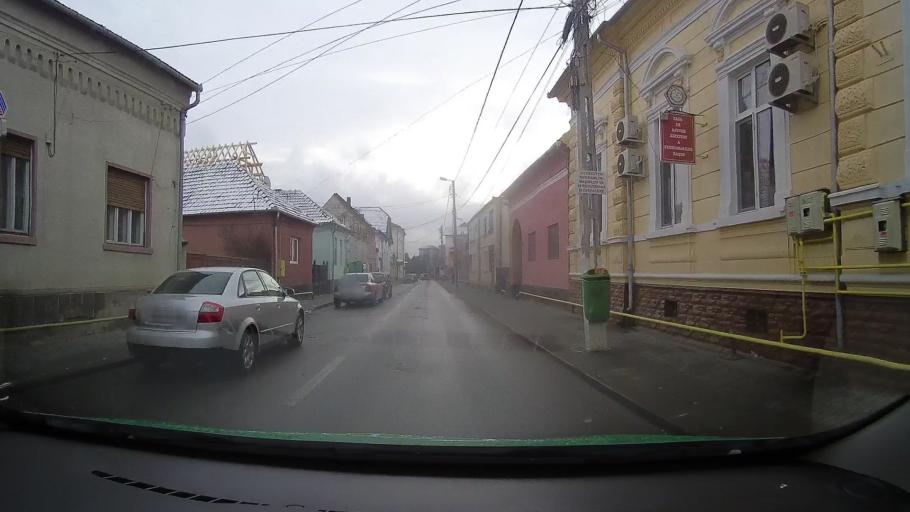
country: RO
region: Hunedoara
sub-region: Oras Hateg
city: Hateg
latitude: 45.6117
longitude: 22.9484
